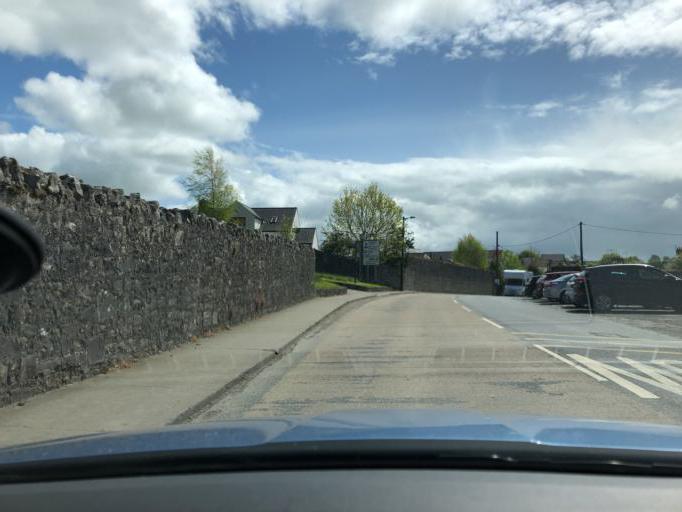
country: IE
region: Munster
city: Cashel
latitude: 52.5185
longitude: -7.8938
